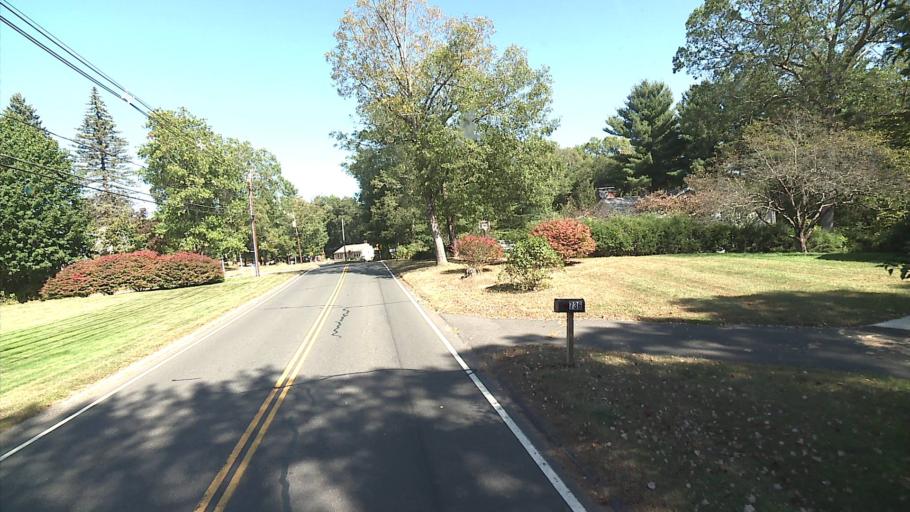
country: US
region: Connecticut
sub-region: Hartford County
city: Glastonbury Center
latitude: 41.6970
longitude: -72.5312
